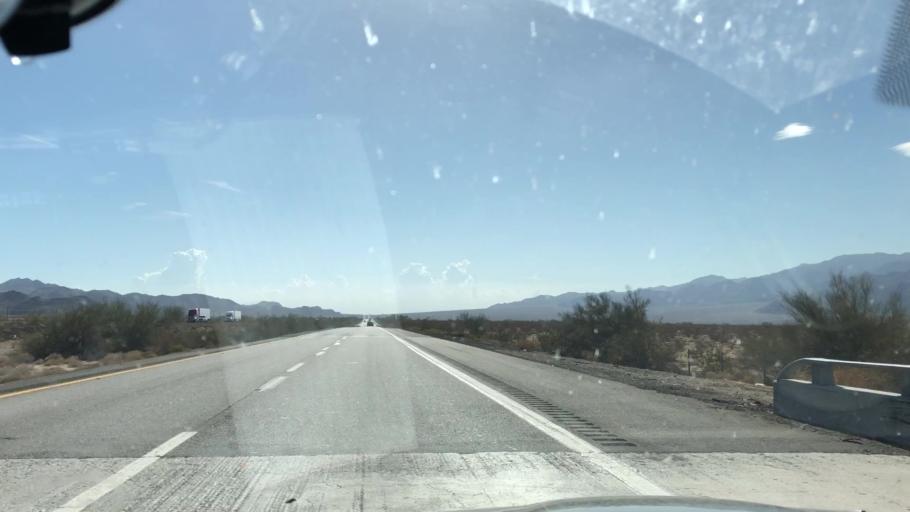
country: US
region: California
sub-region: Imperial County
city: Niland
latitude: 33.6729
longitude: -115.5934
